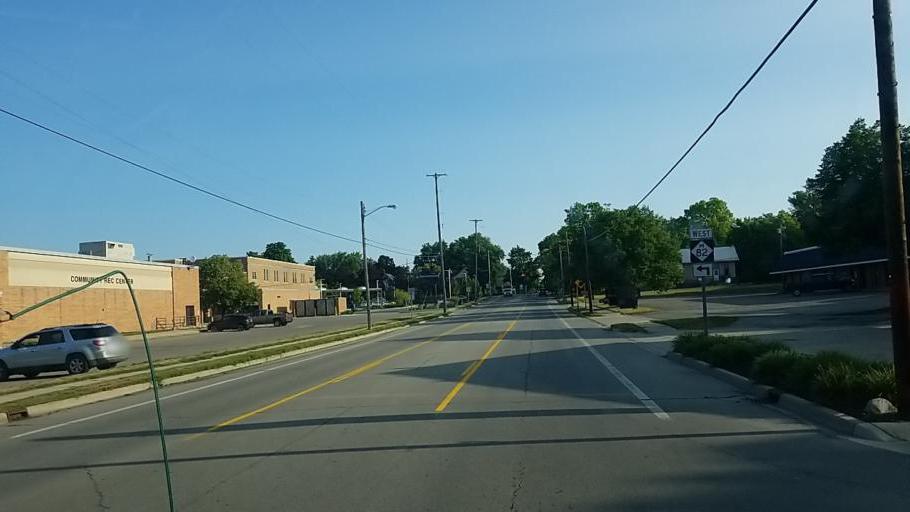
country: US
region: Michigan
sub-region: Newaygo County
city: Fremont
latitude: 43.4653
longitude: -85.9400
